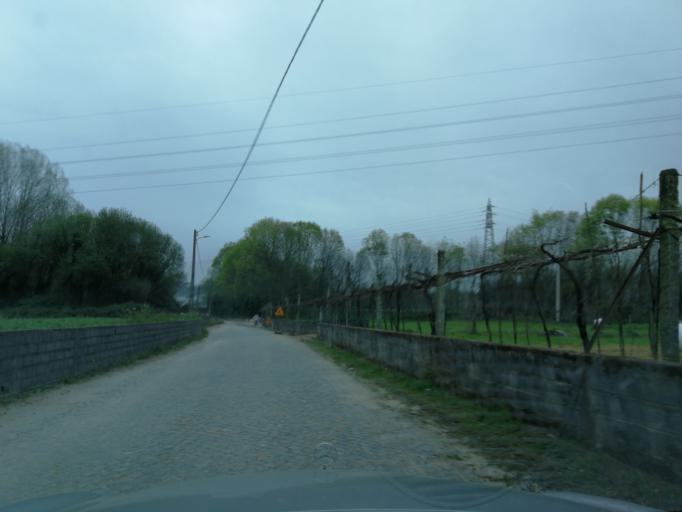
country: PT
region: Braga
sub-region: Braga
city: Braga
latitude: 41.5743
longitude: -8.4382
